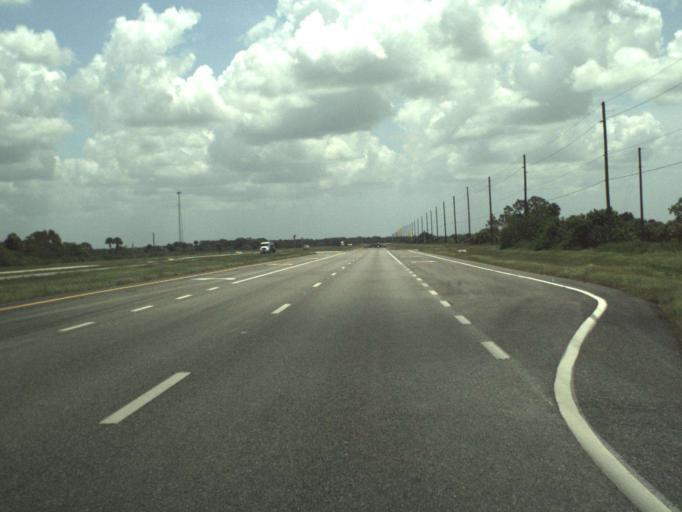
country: US
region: Florida
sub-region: Saint Lucie County
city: Fort Pierce South
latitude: 27.3716
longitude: -80.5900
